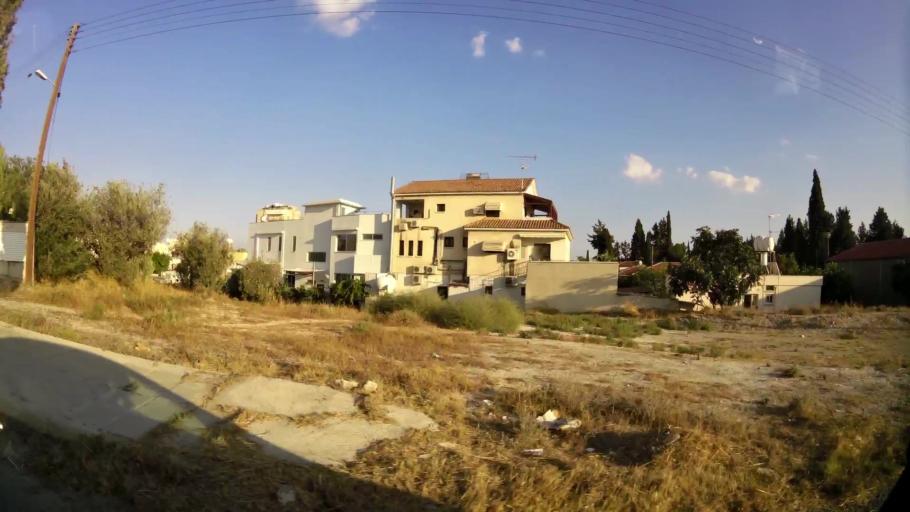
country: CY
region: Larnaka
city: Larnaca
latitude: 34.9263
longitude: 33.6051
